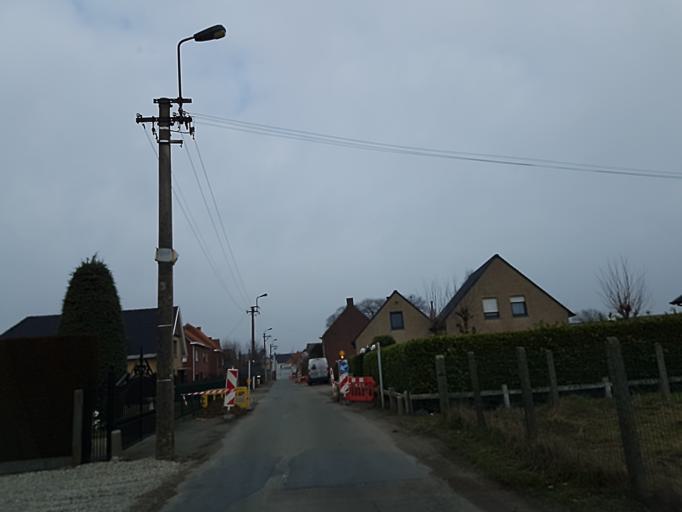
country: BE
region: Flanders
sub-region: Provincie Oost-Vlaanderen
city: Nevele
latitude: 51.0303
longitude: 3.5467
